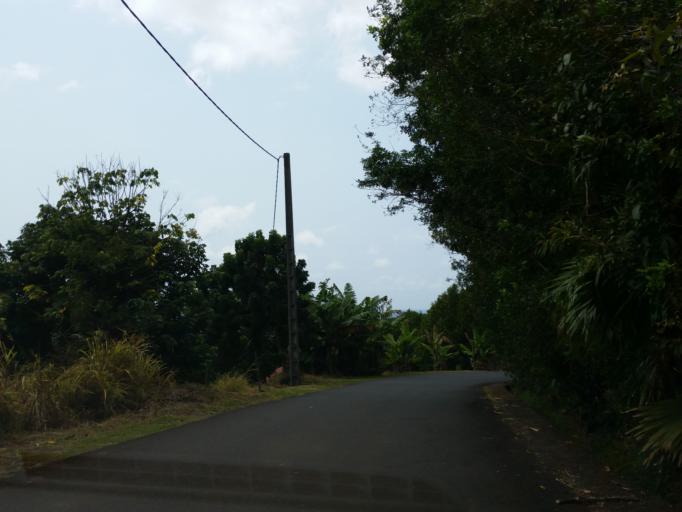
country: RE
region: Reunion
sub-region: Reunion
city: Sainte-Suzanne
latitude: -20.9248
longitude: 55.6065
